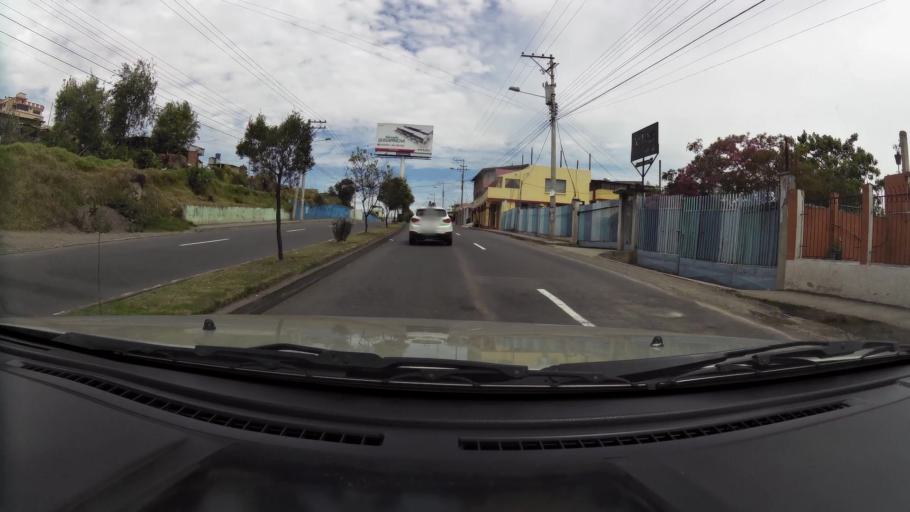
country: EC
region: Cotopaxi
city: San Miguel de Salcedo
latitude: -1.1043
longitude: -78.5910
